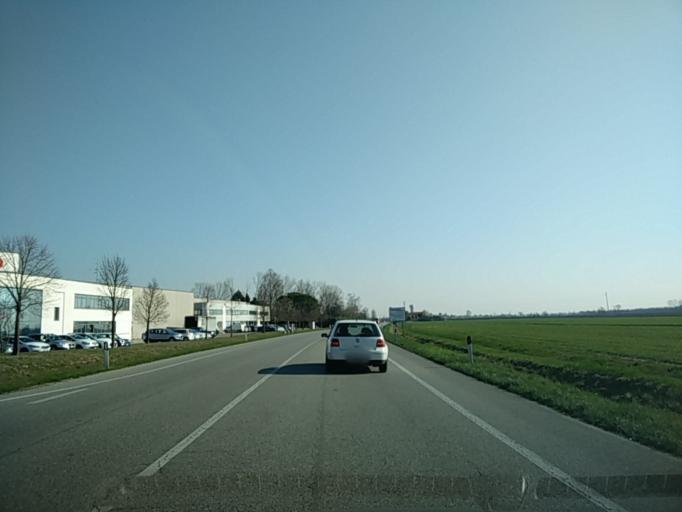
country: IT
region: Friuli Venezia Giulia
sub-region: Provincia di Pordenone
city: Villotta
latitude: 45.8788
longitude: 12.7806
